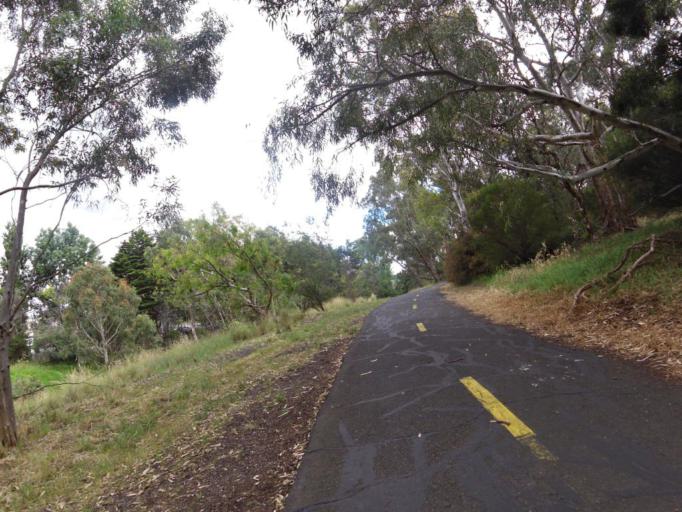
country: AU
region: Victoria
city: Heidelberg West
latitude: -37.7550
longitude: 145.0311
